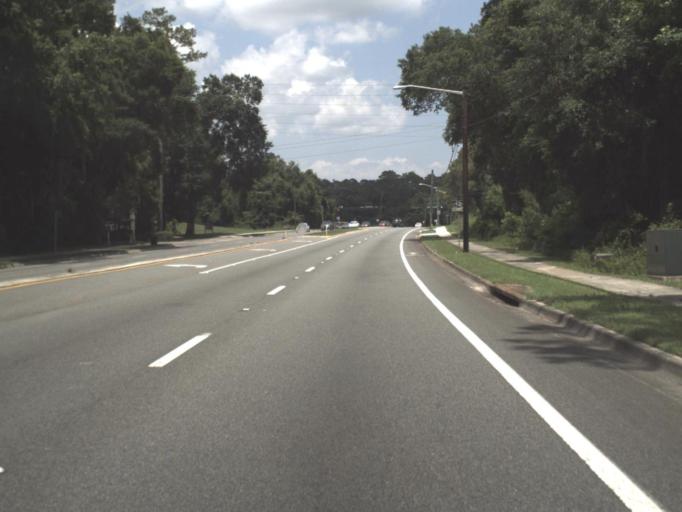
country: US
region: Florida
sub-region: Alachua County
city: Gainesville
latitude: 29.6127
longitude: -82.3576
